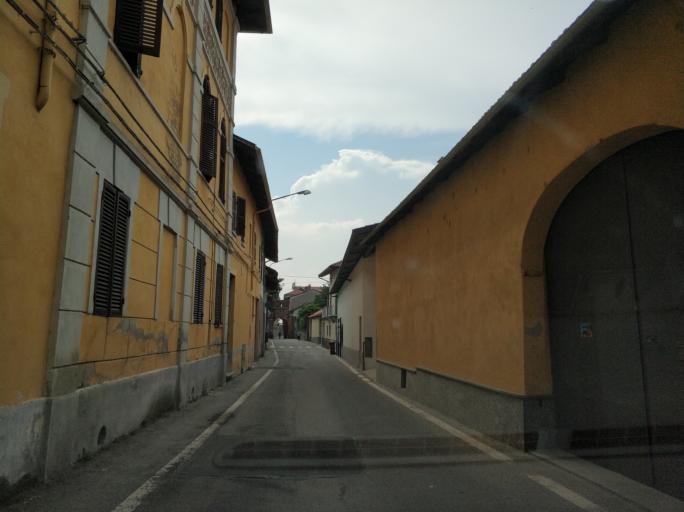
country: IT
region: Piedmont
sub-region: Provincia di Torino
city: Caluso
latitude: 45.3074
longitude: 7.8947
